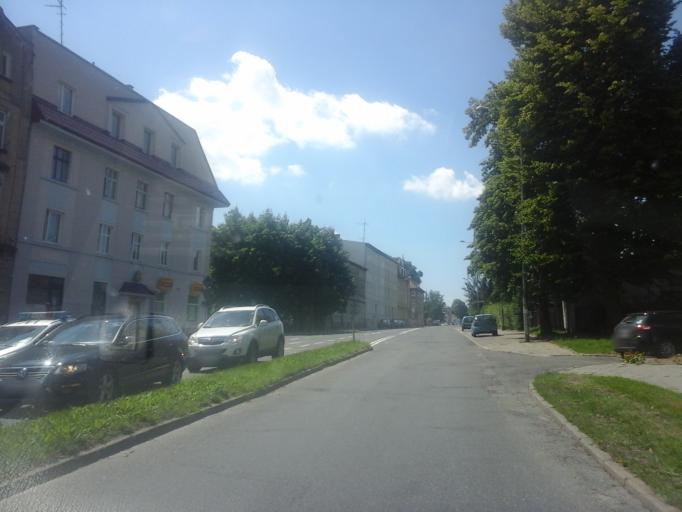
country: PL
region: West Pomeranian Voivodeship
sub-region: Koszalin
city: Koszalin
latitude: 54.1848
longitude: 16.1770
